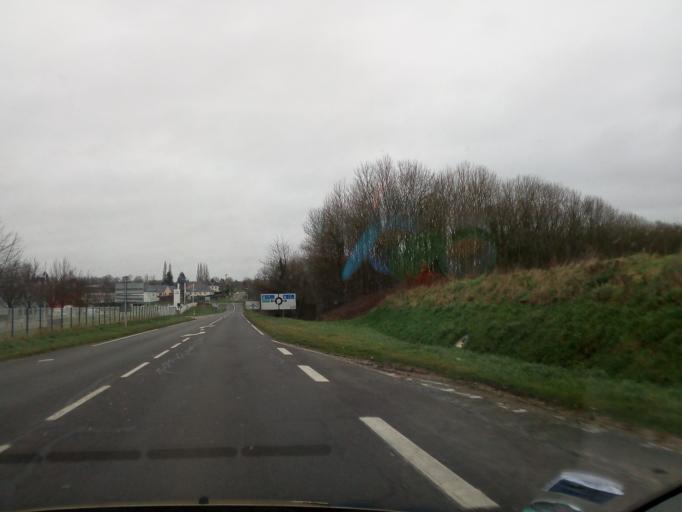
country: FR
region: Haute-Normandie
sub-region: Departement de la Seine-Maritime
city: Auzebosc
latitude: 49.6036
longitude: 0.7399
